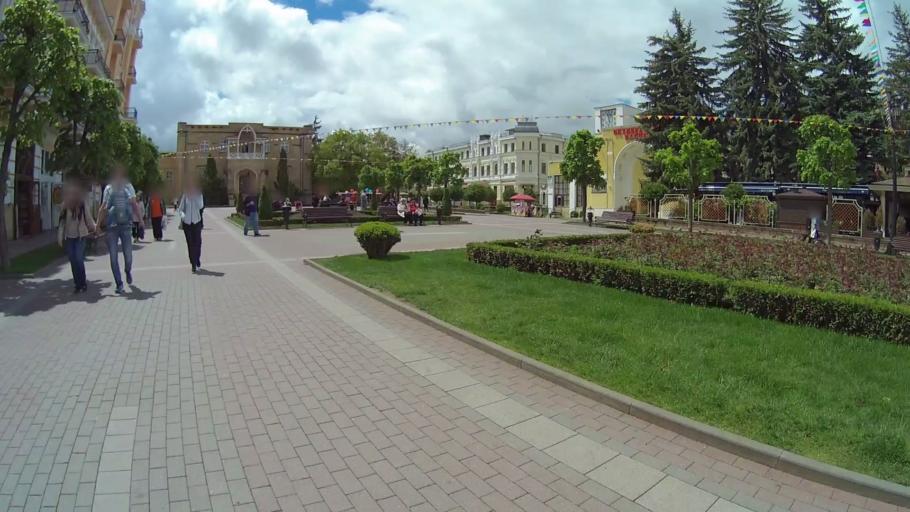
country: RU
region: Stavropol'skiy
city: Kislovodsk
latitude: 43.9013
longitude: 42.7169
